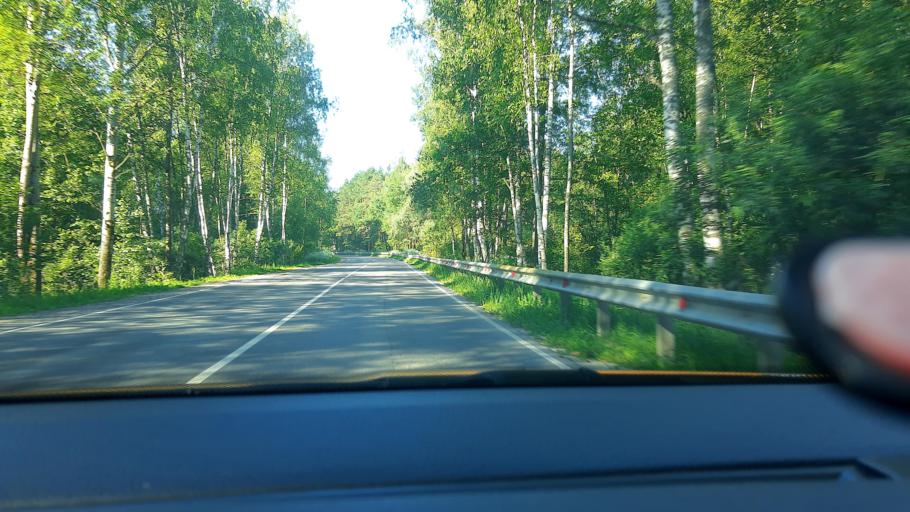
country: RU
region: Moskovskaya
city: Elektrogorsk
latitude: 55.8811
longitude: 38.7018
